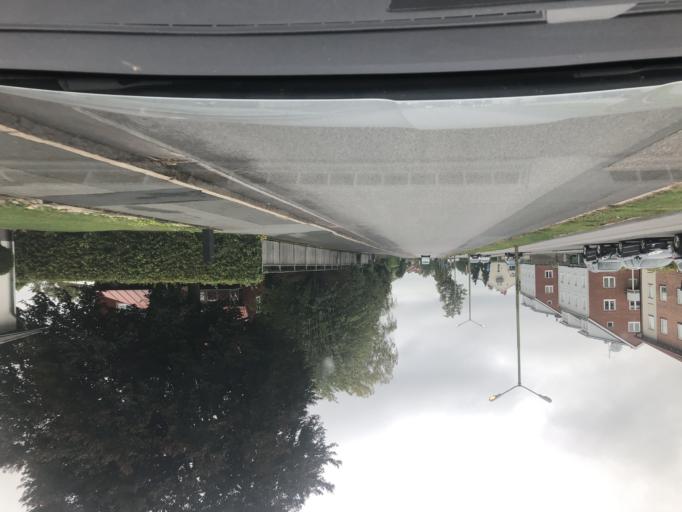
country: SE
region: Joenkoeping
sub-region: Varnamo Kommun
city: Varnamo
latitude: 57.1786
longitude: 14.0325
